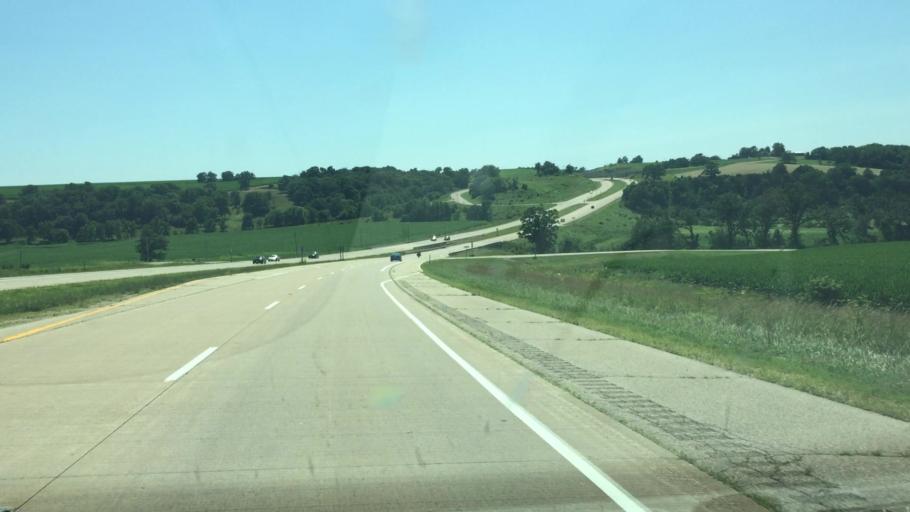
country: US
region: Wisconsin
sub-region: Iowa County
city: Mineral Point
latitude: 42.8266
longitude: -90.2374
